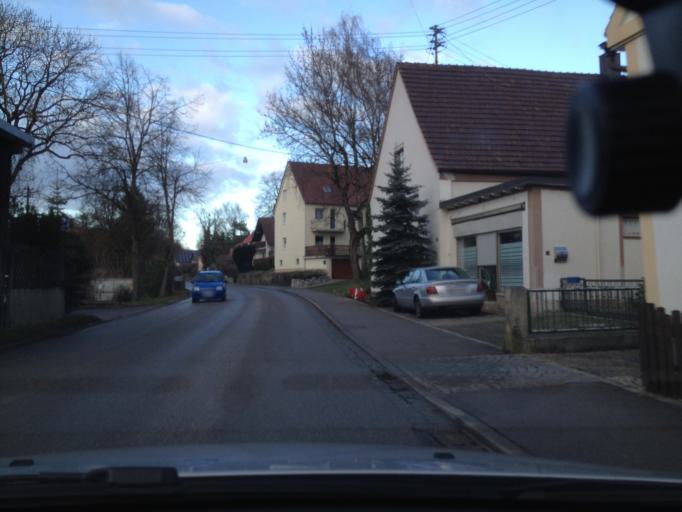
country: DE
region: Bavaria
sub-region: Swabia
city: Langerringen
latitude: 48.1437
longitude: 10.7587
